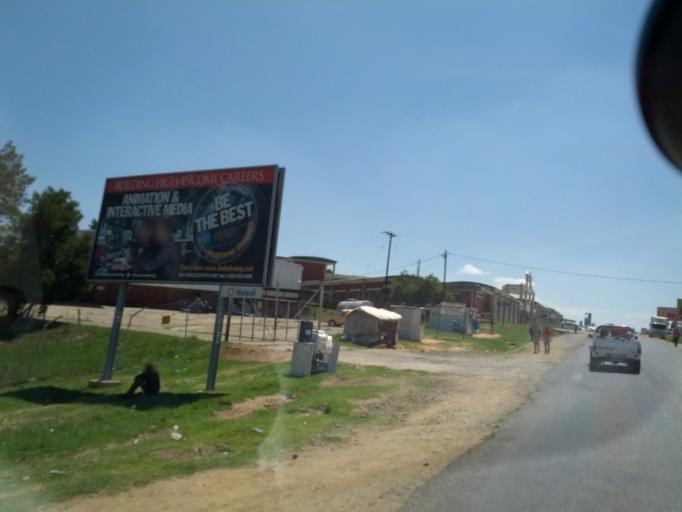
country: LS
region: Butha-Buthe
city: Butha-Buthe
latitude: -28.7703
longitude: 28.2471
